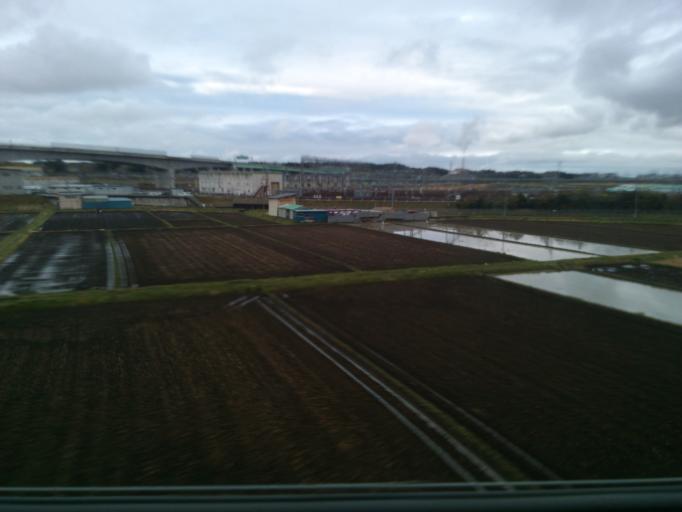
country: JP
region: Miyagi
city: Rifu
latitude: 38.3154
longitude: 140.9665
